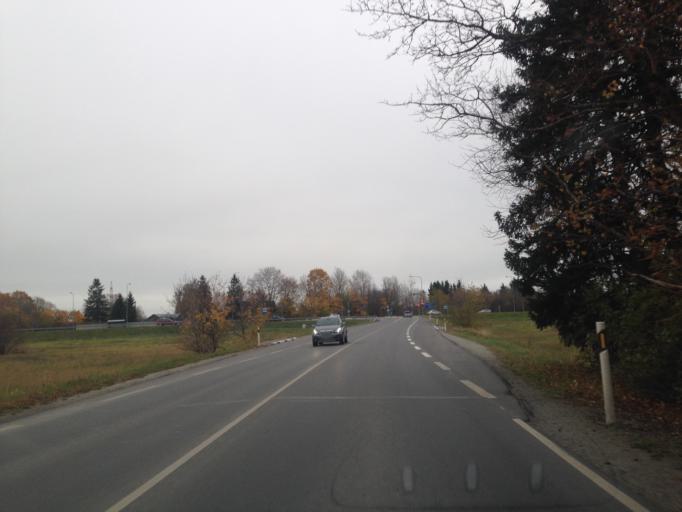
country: EE
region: Harju
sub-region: Harku vald
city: Tabasalu
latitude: 59.3909
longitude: 24.5567
